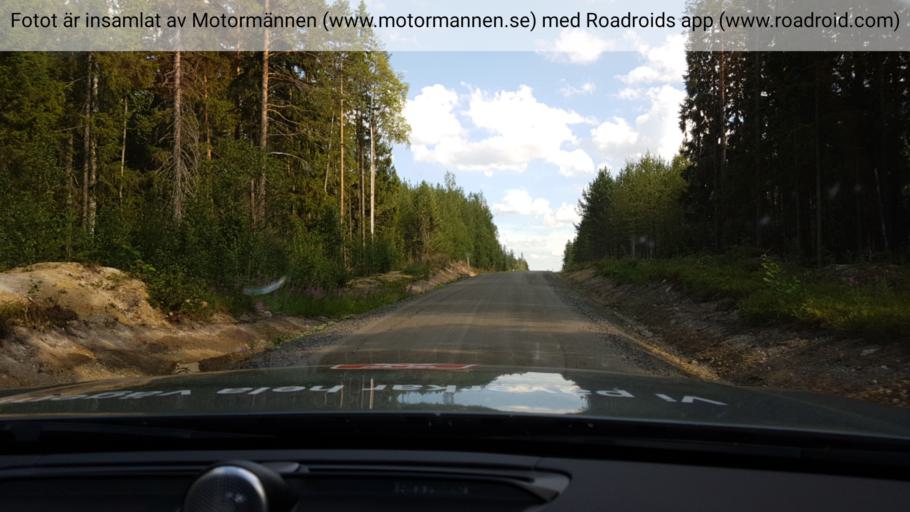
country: SE
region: Vaesterbotten
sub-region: Dorotea Kommun
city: Dorotea
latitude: 63.9405
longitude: 16.0856
